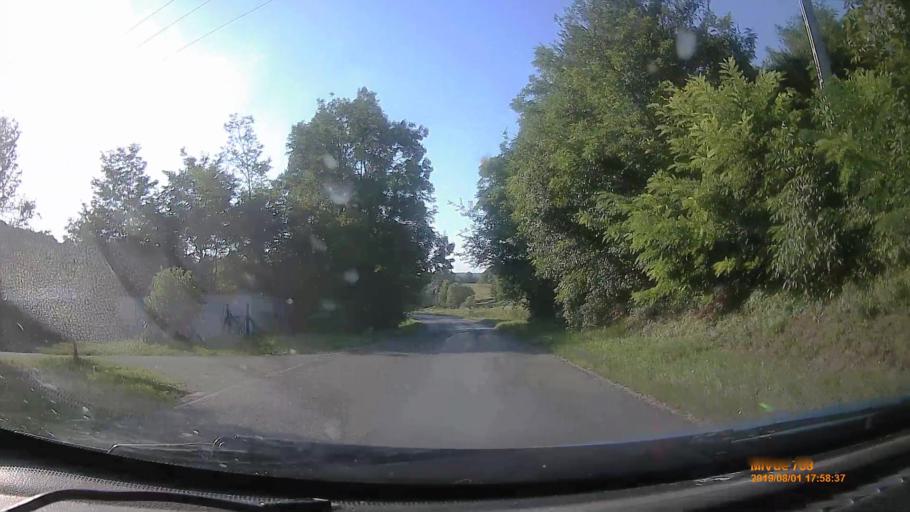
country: HU
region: Baranya
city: Sasd
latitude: 46.2020
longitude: 18.1122
